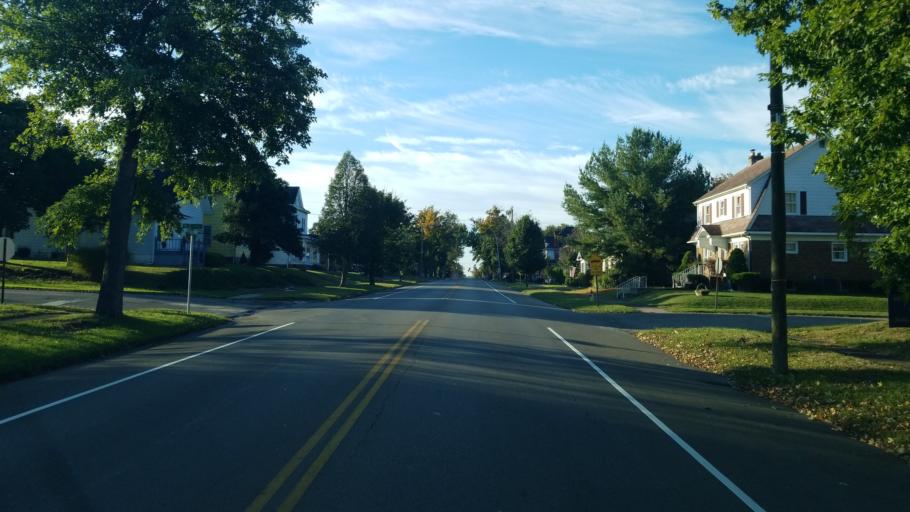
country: US
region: Ohio
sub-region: Jackson County
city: Wellston
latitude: 39.1270
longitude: -82.5326
